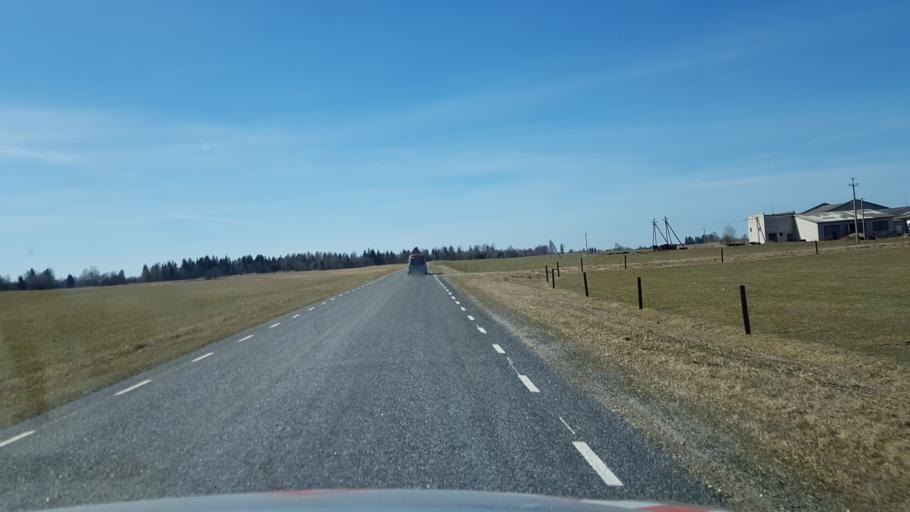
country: EE
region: Laeaene-Virumaa
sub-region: Vinni vald
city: Vinni
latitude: 59.0969
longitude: 26.5181
